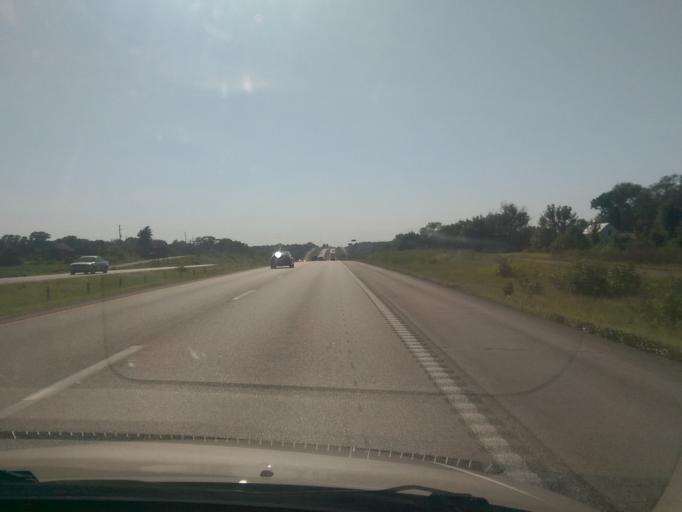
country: US
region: Missouri
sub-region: Saline County
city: Sweet Springs
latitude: 38.9743
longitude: -93.3519
